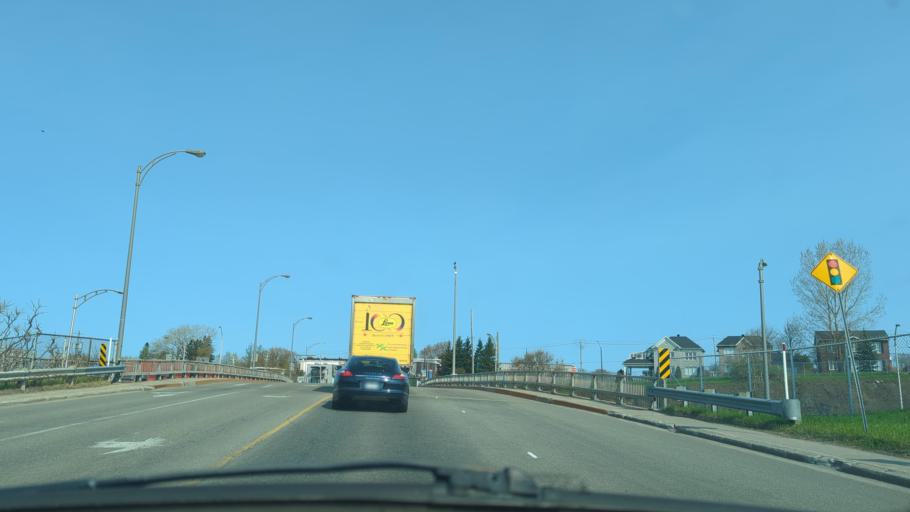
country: CA
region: Quebec
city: Quebec
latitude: 46.8530
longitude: -71.2260
